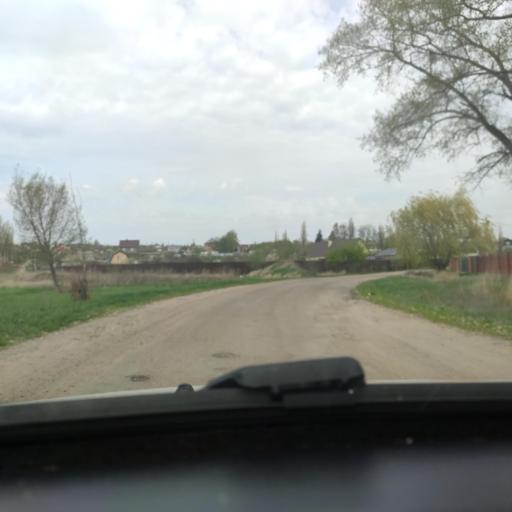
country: RU
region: Voronezj
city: Pridonskoy
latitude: 51.7287
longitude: 39.0583
